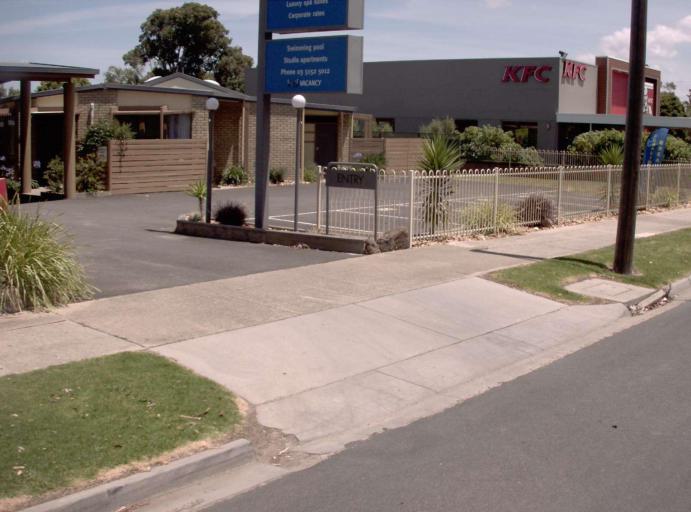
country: AU
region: Victoria
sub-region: East Gippsland
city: Bairnsdale
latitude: -37.8280
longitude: 147.6228
